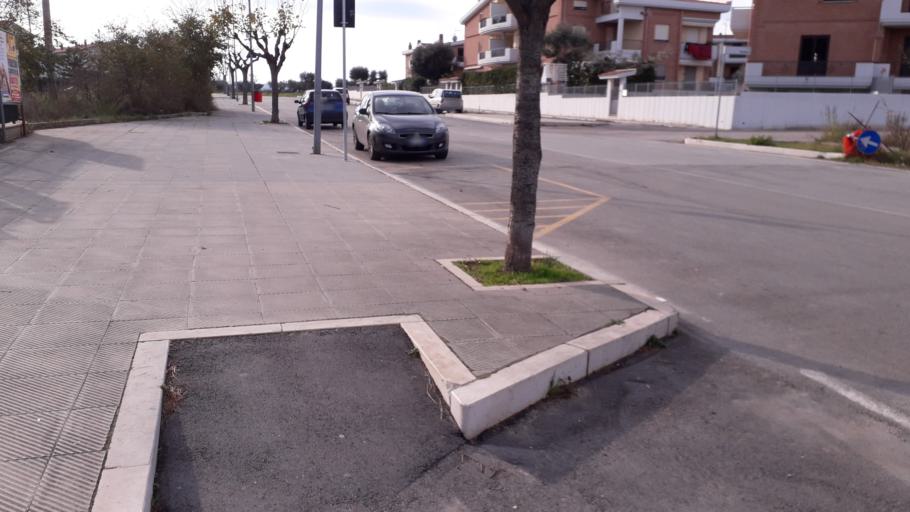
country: IT
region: Molise
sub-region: Provincia di Campobasso
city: Campomarino
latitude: 41.9518
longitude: 15.0318
